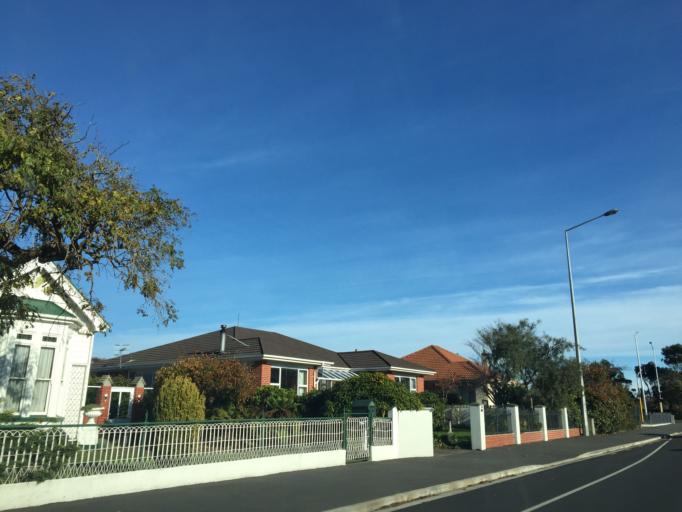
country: NZ
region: Southland
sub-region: Invercargill City
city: Invercargill
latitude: -46.4086
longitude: 168.3626
